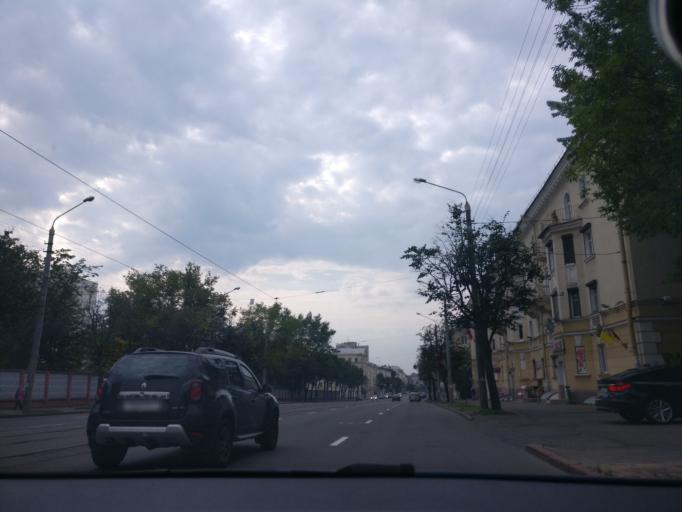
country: BY
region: Minsk
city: Minsk
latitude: 53.9322
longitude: 27.6004
